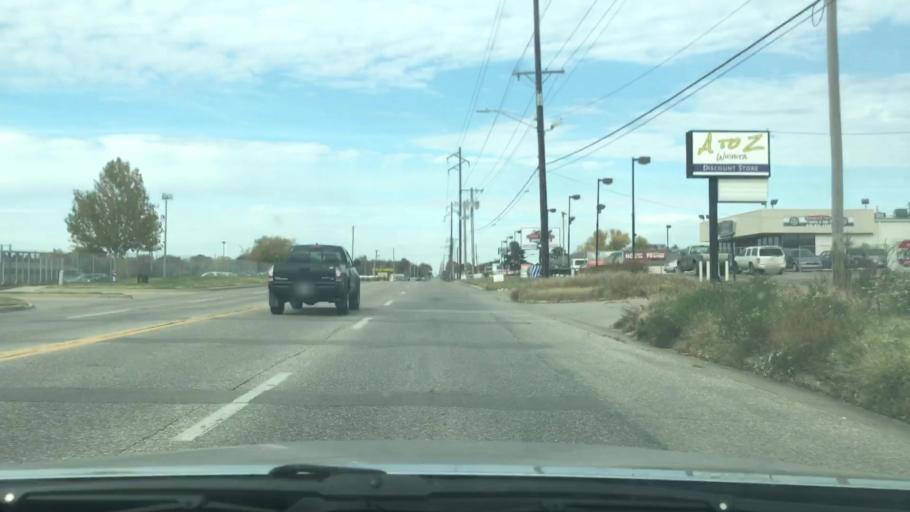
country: US
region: Kansas
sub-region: Sedgwick County
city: Wichita
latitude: 37.6443
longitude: -97.2804
